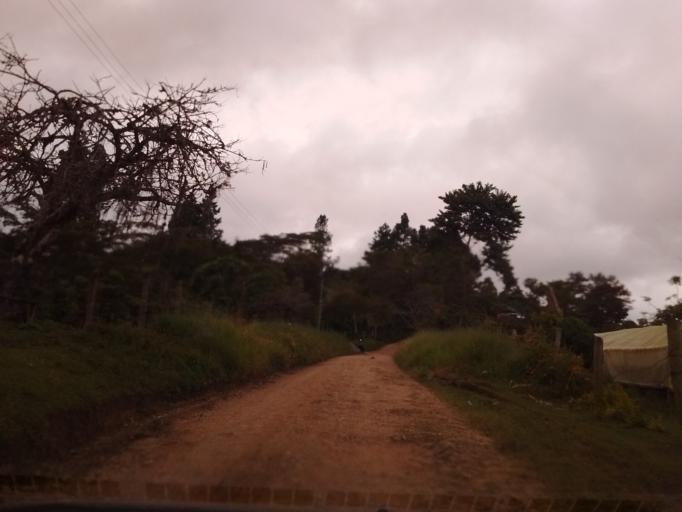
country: CO
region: Huila
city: San Agustin
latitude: 1.9054
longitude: -76.3015
